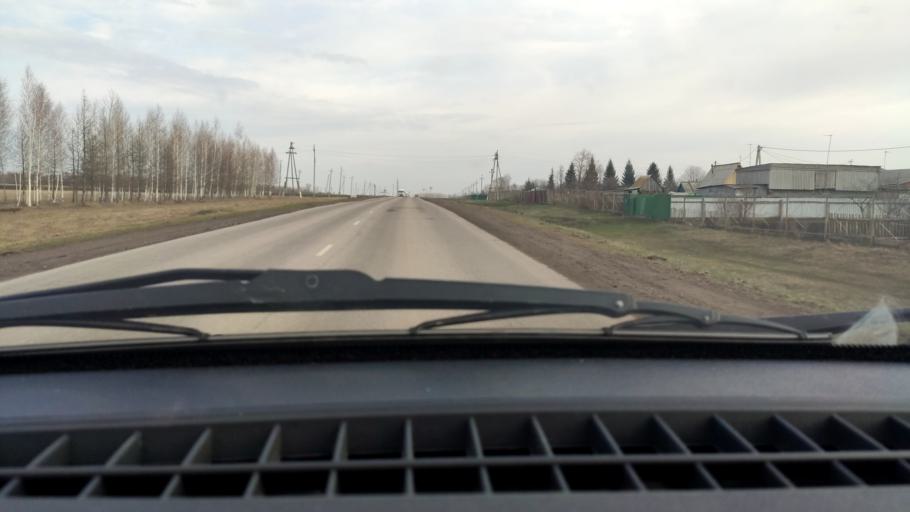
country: RU
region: Bashkortostan
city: Davlekanovo
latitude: 54.3754
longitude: 55.1955
